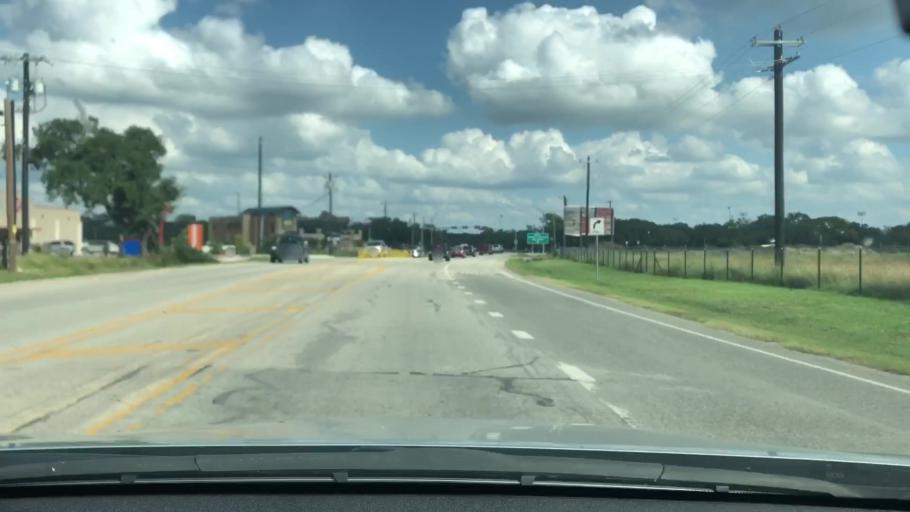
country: US
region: Texas
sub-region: Kendall County
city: Boerne
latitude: 29.7890
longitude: -98.7075
